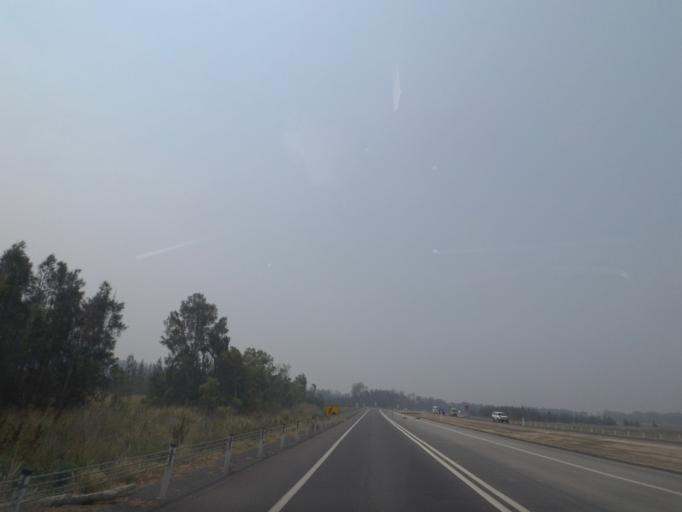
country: AU
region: New South Wales
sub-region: Ballina
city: Ballina
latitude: -28.8719
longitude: 153.4905
